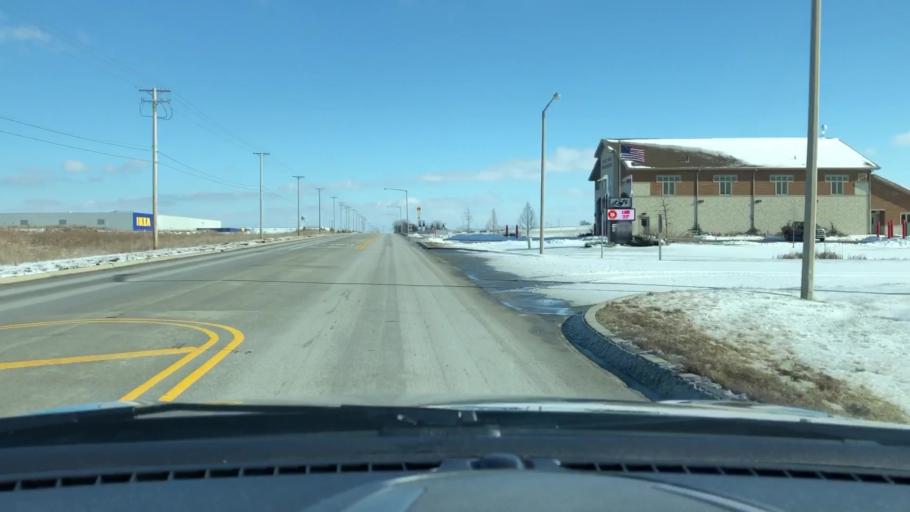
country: US
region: Illinois
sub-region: Will County
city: Preston Heights
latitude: 41.4810
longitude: -88.0685
